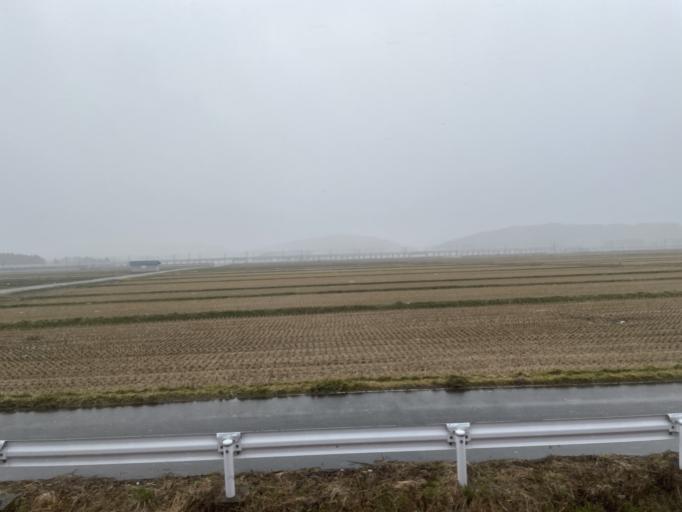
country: JP
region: Aomori
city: Aomori Shi
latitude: 40.8776
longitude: 140.6775
